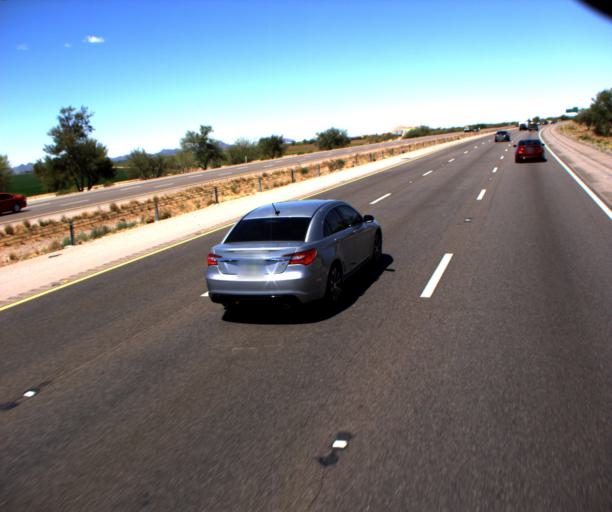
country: US
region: Arizona
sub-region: Pima County
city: Marana
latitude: 32.4918
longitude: -111.2580
